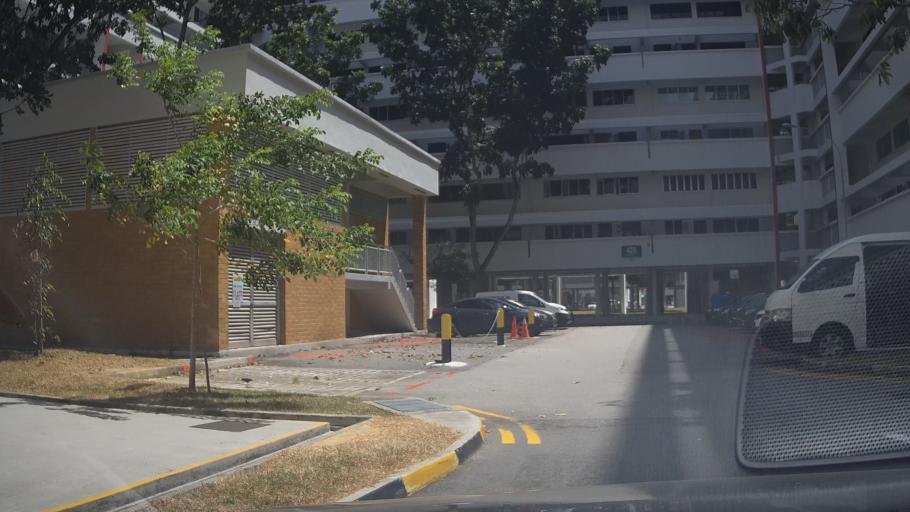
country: SG
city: Singapore
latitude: 1.3594
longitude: 103.9486
